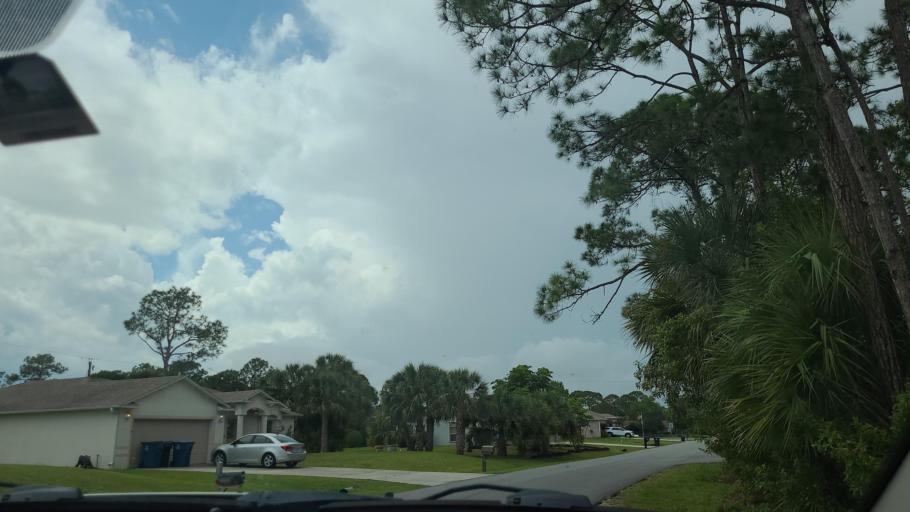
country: US
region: Florida
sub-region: Brevard County
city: Grant-Valkaria
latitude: 27.9443
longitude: -80.6273
